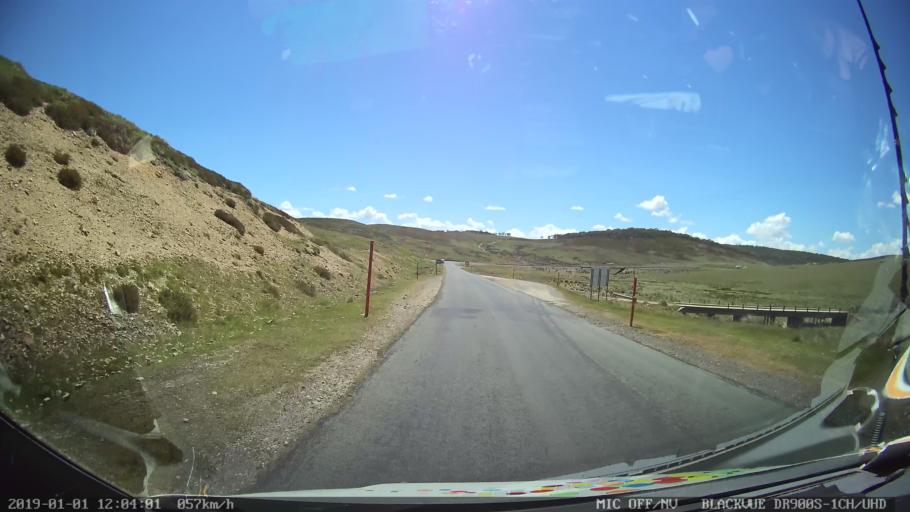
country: AU
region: New South Wales
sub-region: Snowy River
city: Jindabyne
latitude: -35.8687
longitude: 148.4931
